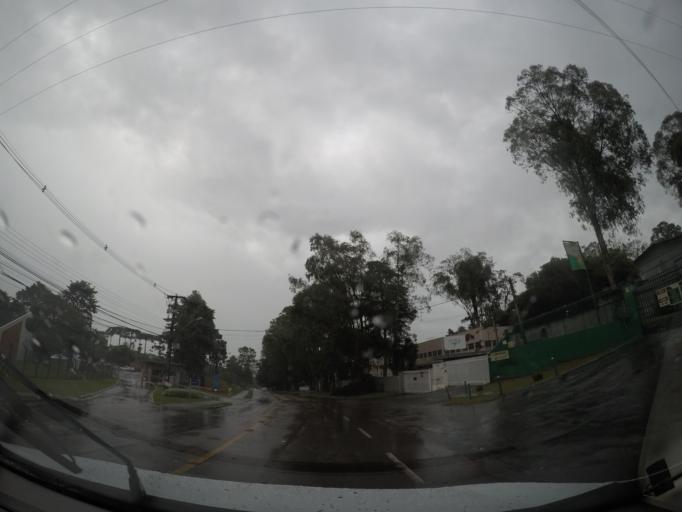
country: BR
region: Parana
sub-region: Curitiba
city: Curitiba
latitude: -25.4521
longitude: -49.3651
